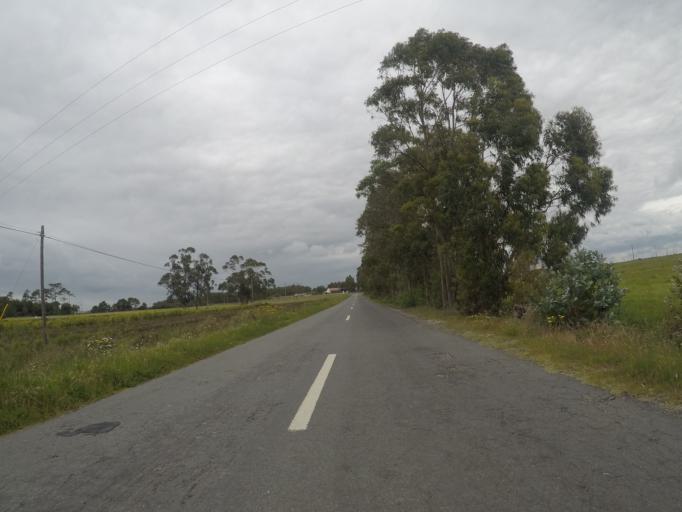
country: PT
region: Beja
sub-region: Odemira
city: Sao Teotonio
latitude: 37.5890
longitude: -8.7778
